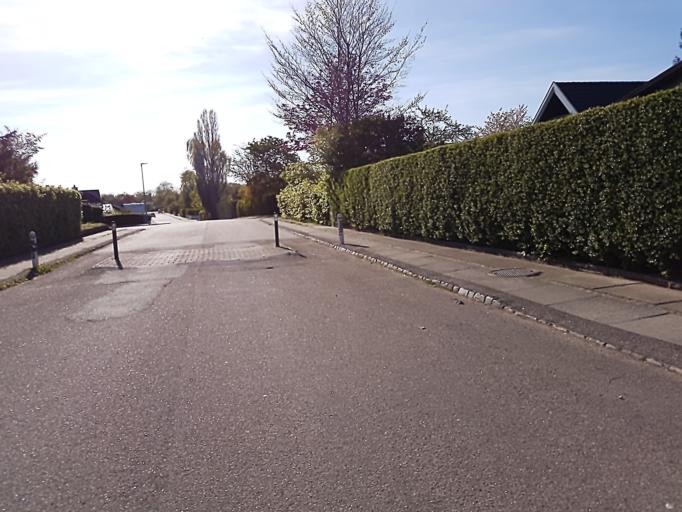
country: DK
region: Capital Region
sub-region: Egedal Kommune
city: Olstykke
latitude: 55.7924
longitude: 12.1455
